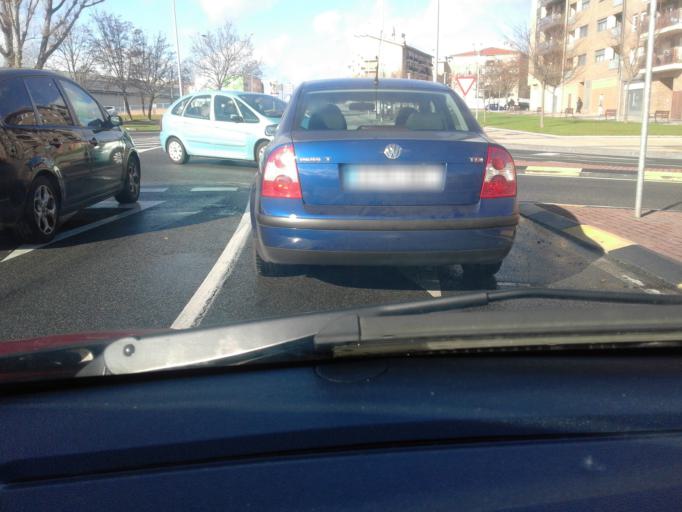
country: ES
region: Navarre
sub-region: Provincia de Navarra
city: Berriozar
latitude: 42.8248
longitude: -1.6575
